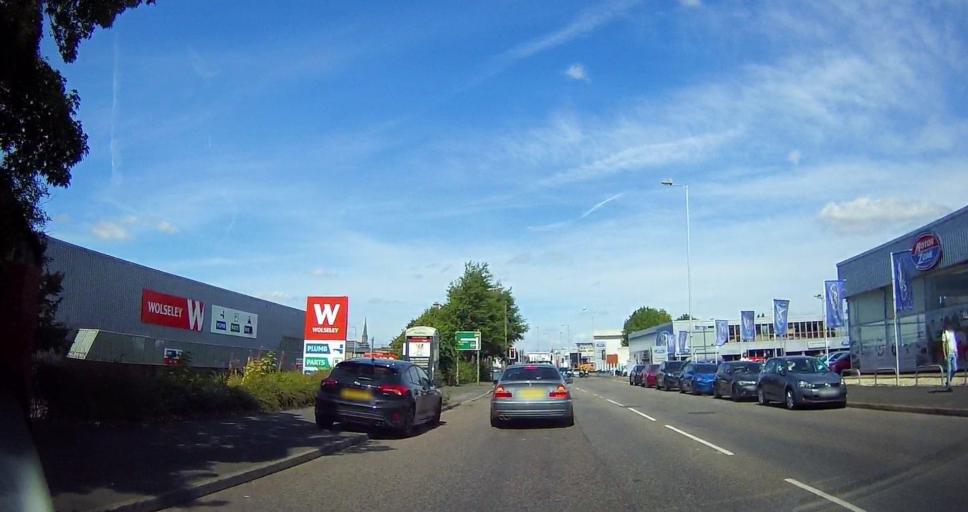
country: GB
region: England
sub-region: Wolverhampton
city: Wolverhampton
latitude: 52.5763
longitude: -2.1242
